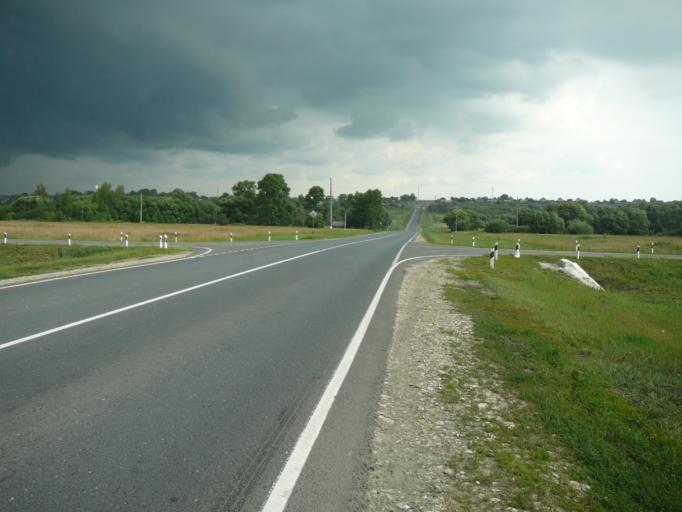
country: RU
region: Penza
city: Issa
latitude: 53.7373
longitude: 44.7660
